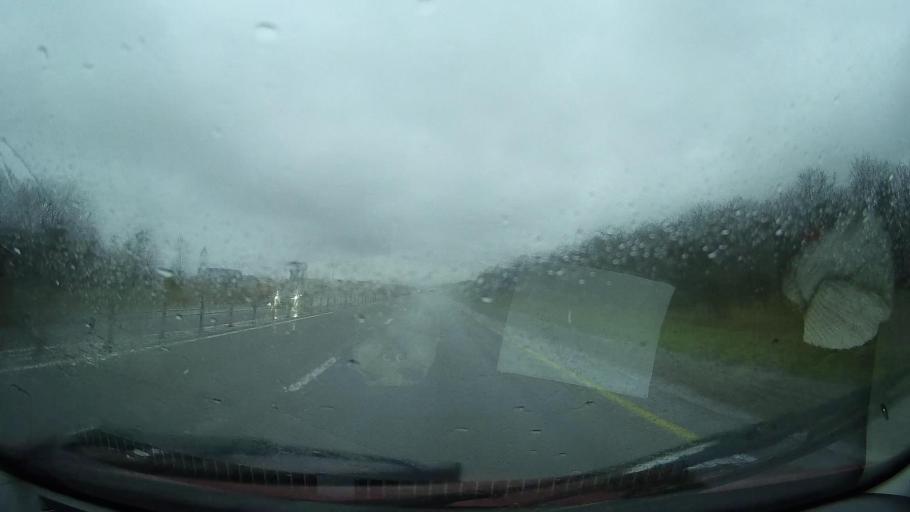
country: RU
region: Stavropol'skiy
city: Nevinnomyssk
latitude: 44.6393
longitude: 41.9768
